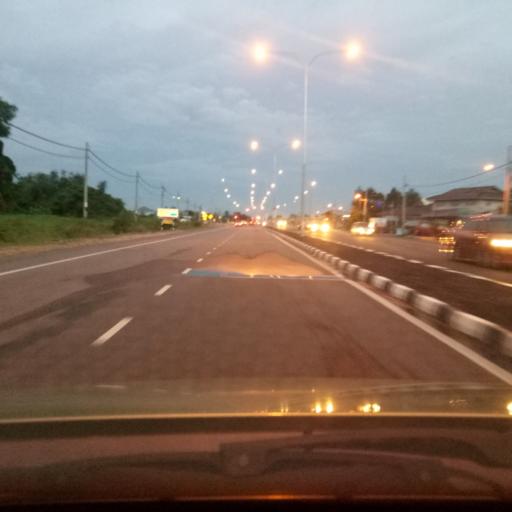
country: MY
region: Kedah
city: Alor Setar
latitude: 6.0943
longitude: 100.3818
